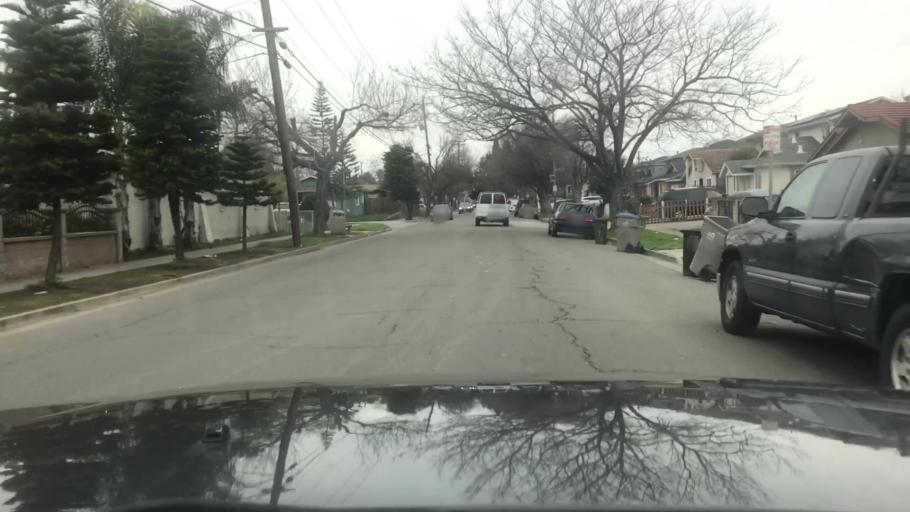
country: US
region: California
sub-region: Santa Clara County
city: Seven Trees
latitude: 37.3200
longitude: -121.8203
